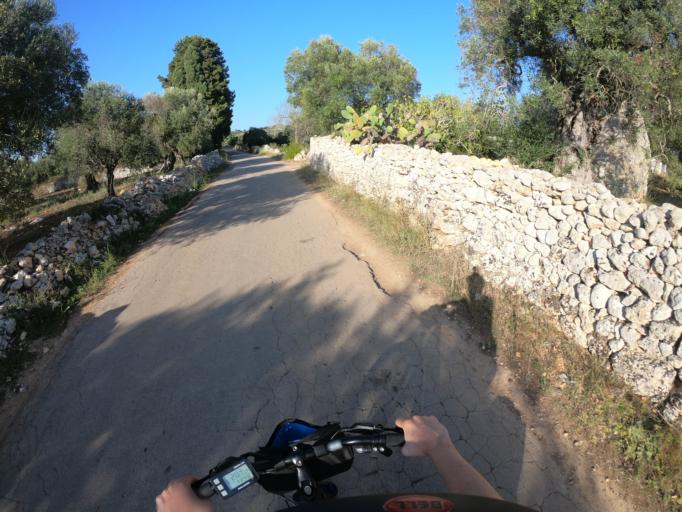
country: IT
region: Apulia
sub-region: Provincia di Lecce
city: Castrignano del Capo
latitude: 39.8246
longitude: 18.3566
